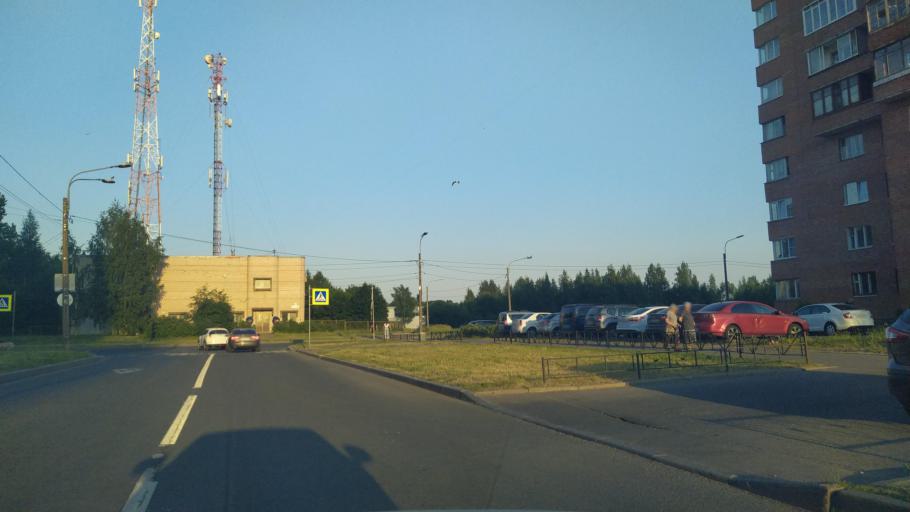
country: RU
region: St.-Petersburg
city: Kronshtadt
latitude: 60.0089
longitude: 29.7247
